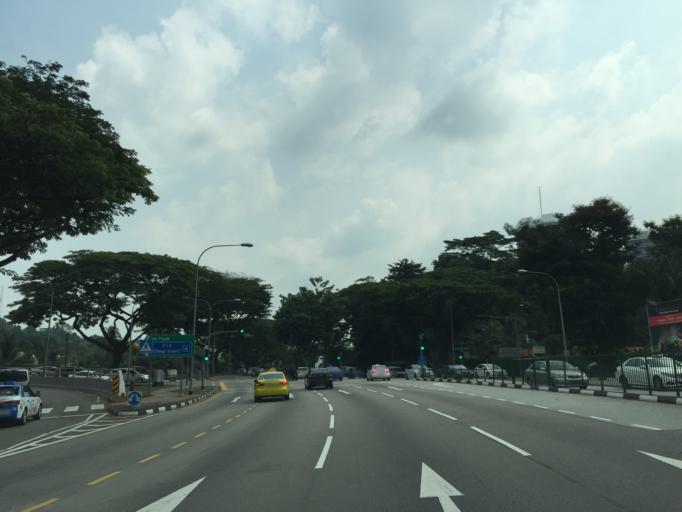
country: SG
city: Singapore
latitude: 1.3294
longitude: 103.8403
